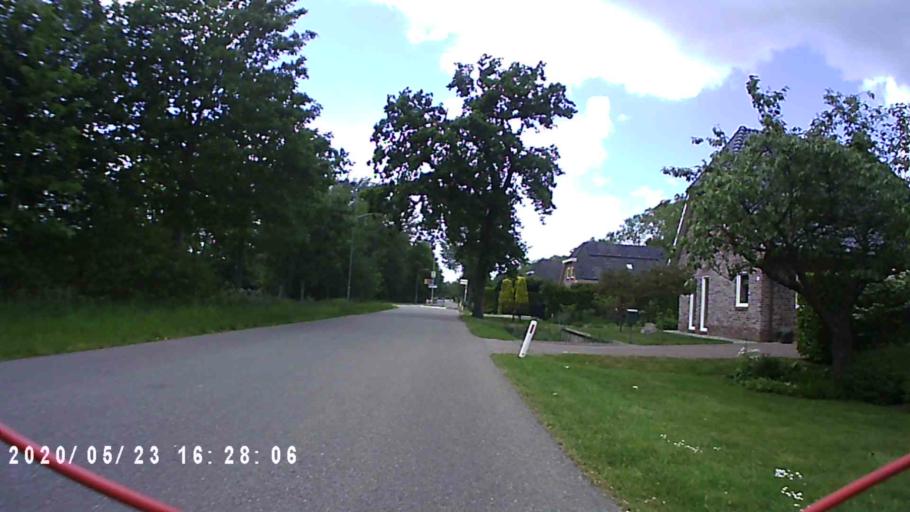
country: NL
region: Groningen
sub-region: Gemeente Appingedam
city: Appingedam
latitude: 53.2704
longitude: 6.8462
